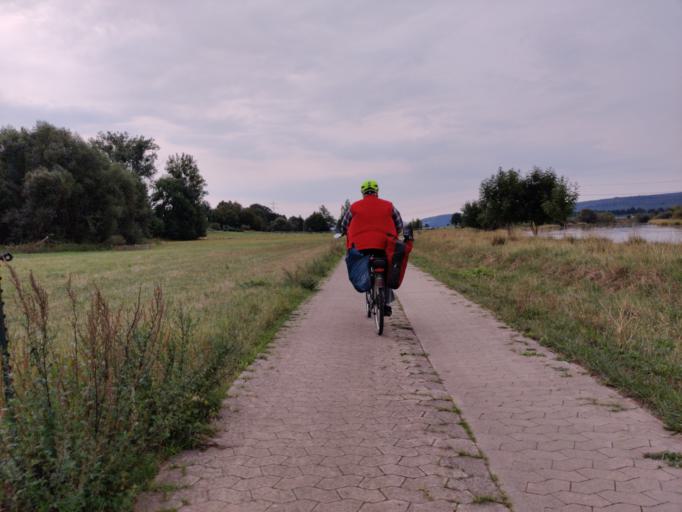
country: DE
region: Lower Saxony
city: Hehlen
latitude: 52.0304
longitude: 9.4302
